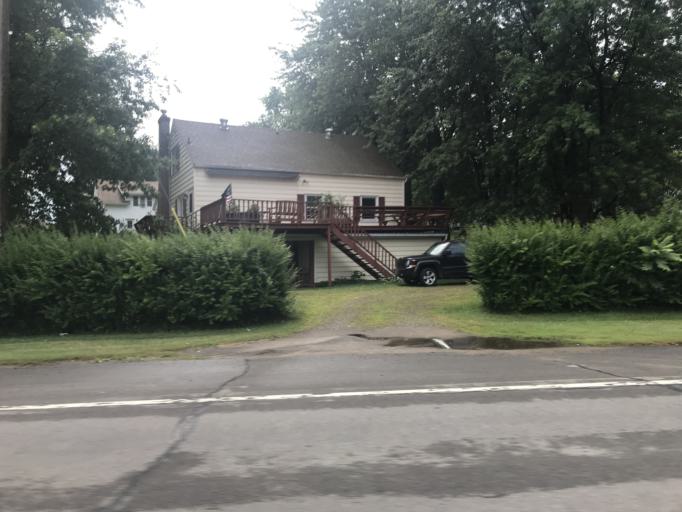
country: US
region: New York
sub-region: Chautauqua County
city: Silver Creek
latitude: 42.5506
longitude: -79.1615
